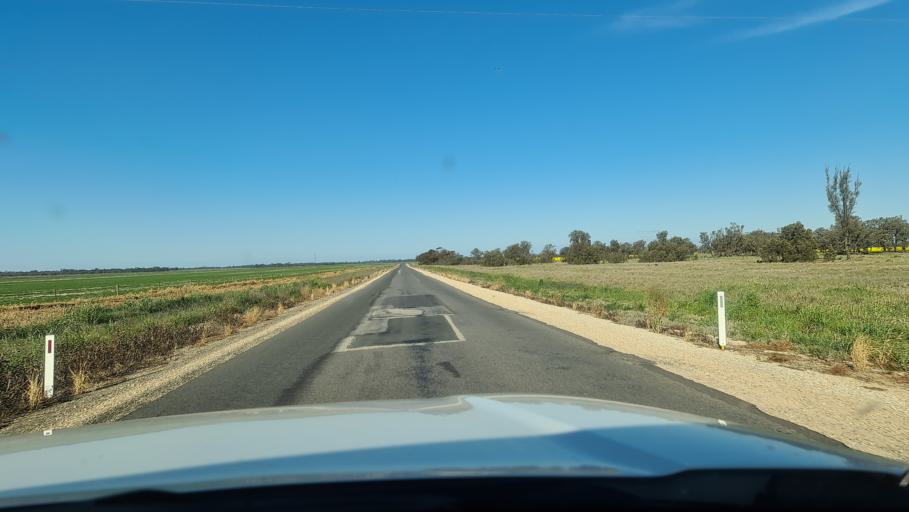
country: AU
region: Victoria
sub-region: Horsham
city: Horsham
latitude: -36.4492
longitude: 142.5587
